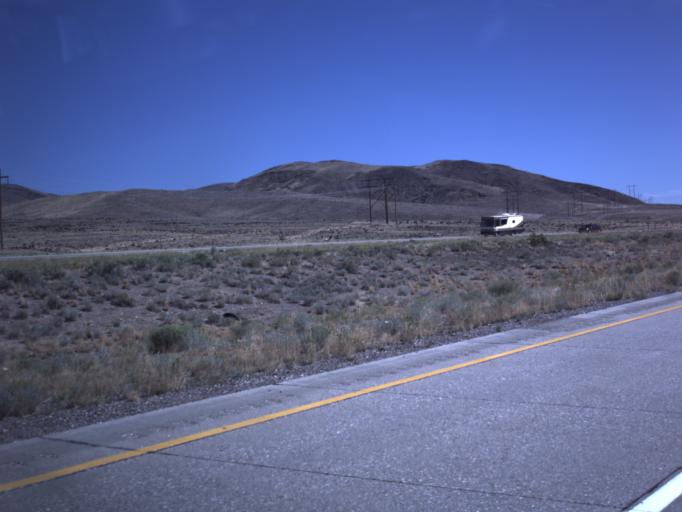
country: US
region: Utah
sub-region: Sevier County
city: Monroe
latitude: 38.6580
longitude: -112.1991
